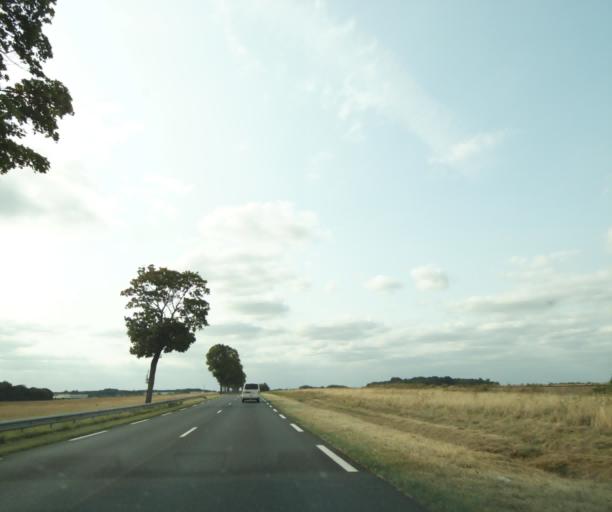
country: FR
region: Centre
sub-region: Departement d'Indre-et-Loire
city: Truyes
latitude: 47.2489
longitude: 0.8527
